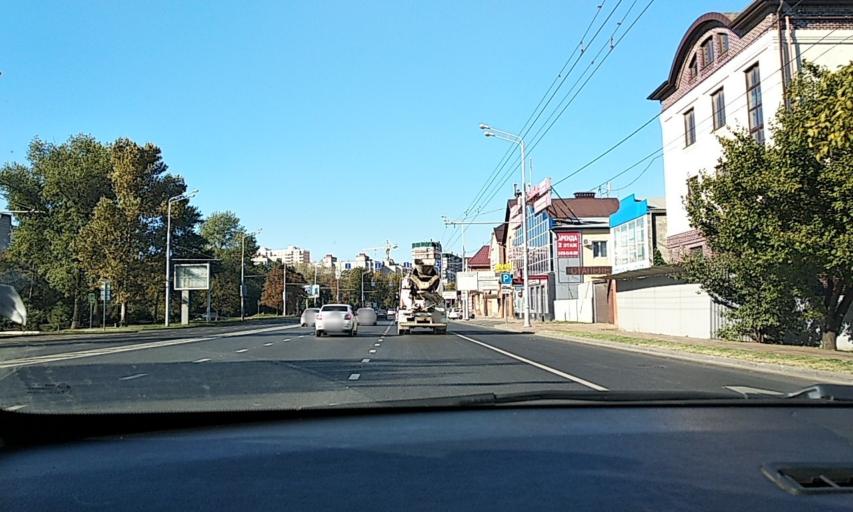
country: RU
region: Krasnodarskiy
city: Pashkovskiy
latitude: 45.0130
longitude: 39.0778
